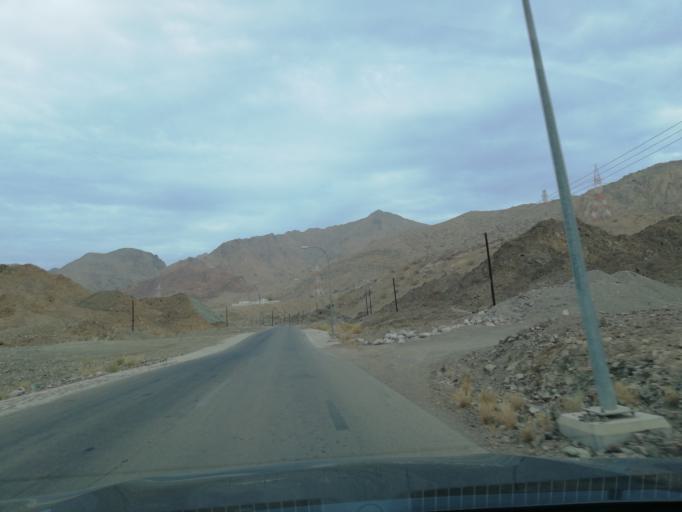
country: OM
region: Muhafazat Masqat
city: Bawshar
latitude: 23.4860
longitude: 58.3382
